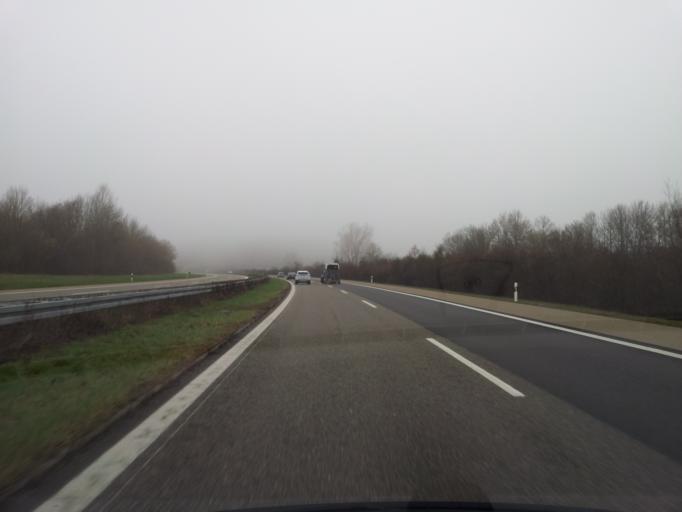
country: DE
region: Baden-Wuerttemberg
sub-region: Freiburg Region
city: Volkertshausen
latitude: 47.8117
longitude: 8.8538
